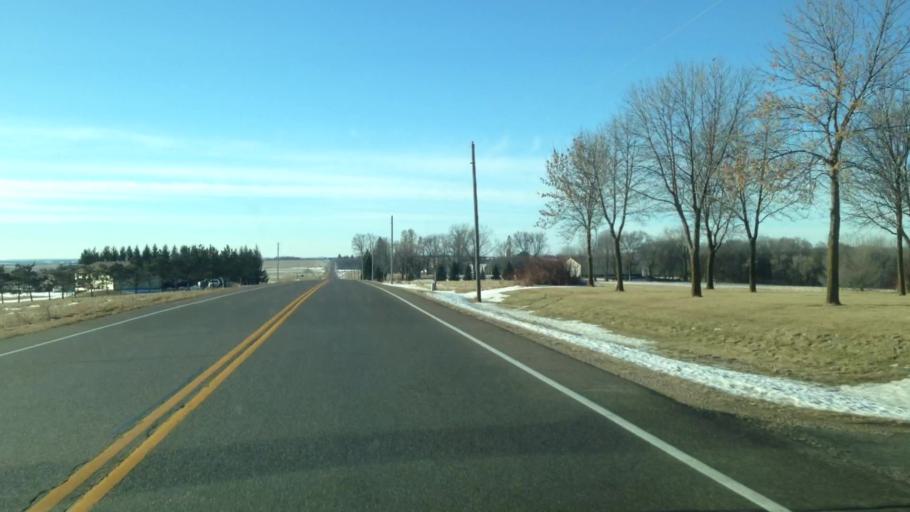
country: US
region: Minnesota
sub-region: Dakota County
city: Farmington
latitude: 44.5837
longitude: -93.0221
